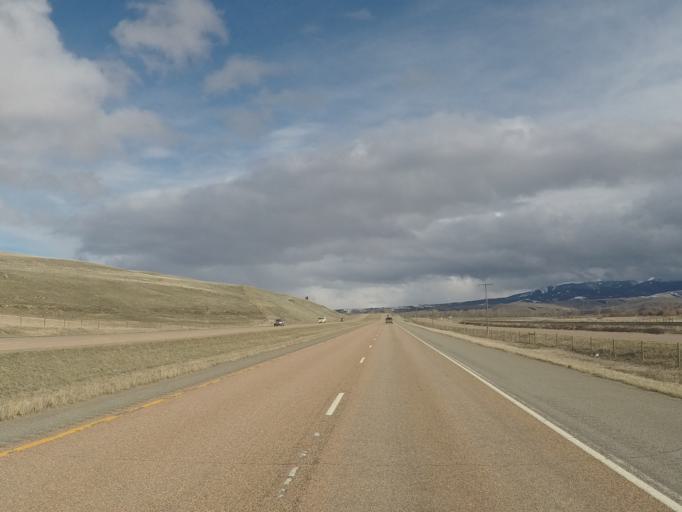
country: US
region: Montana
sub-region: Granite County
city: Philipsburg
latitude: 46.6539
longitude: -113.1259
